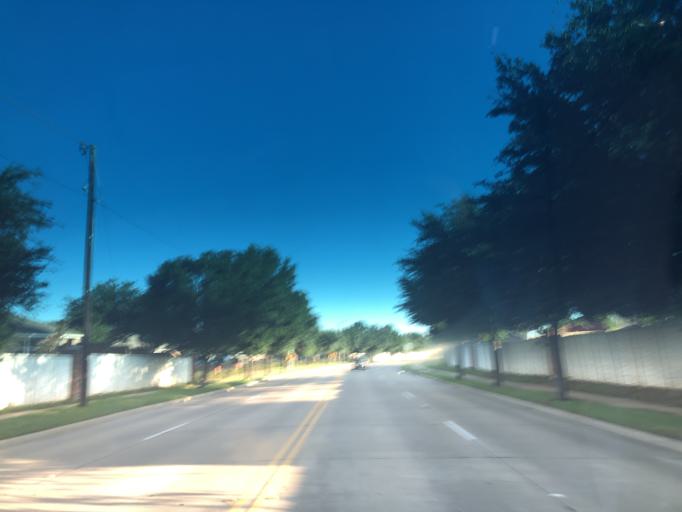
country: US
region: Texas
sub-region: Dallas County
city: Grand Prairie
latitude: 32.7022
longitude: -97.0189
